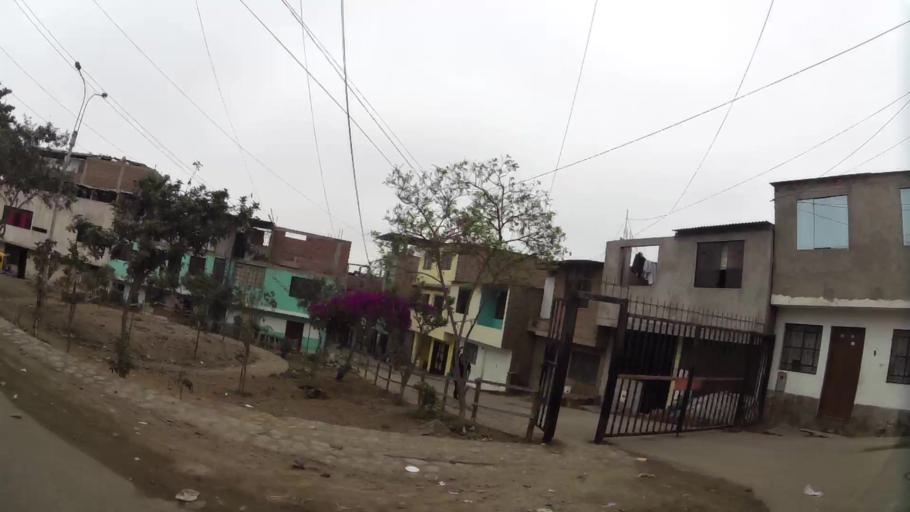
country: PE
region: Lima
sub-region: Lima
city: Surco
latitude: -12.1652
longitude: -76.9581
